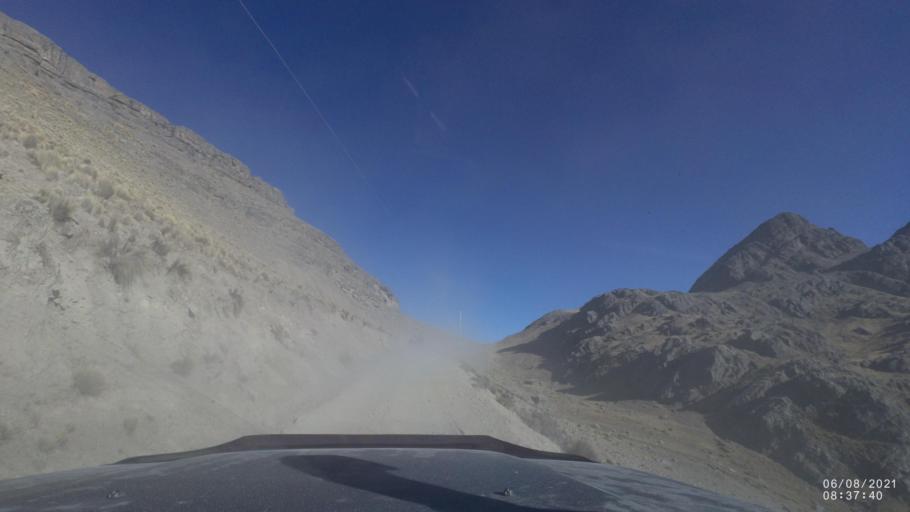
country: BO
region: Cochabamba
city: Sipe Sipe
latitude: -17.1749
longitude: -66.3902
